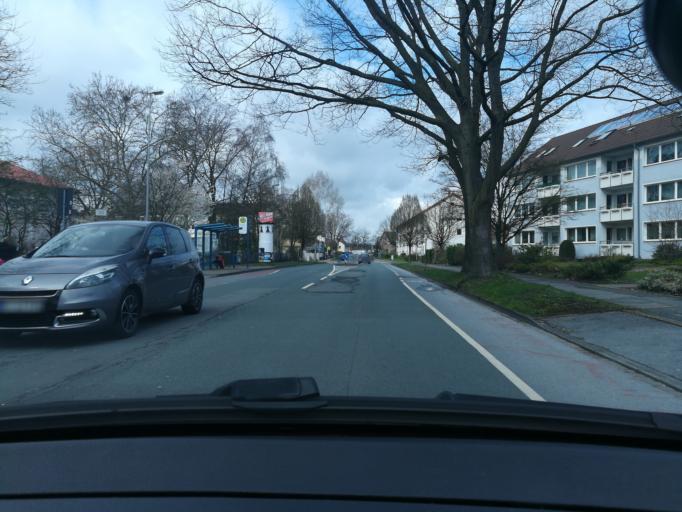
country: DE
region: North Rhine-Westphalia
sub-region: Regierungsbezirk Detmold
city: Oerlinghausen
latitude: 51.9490
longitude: 8.5797
